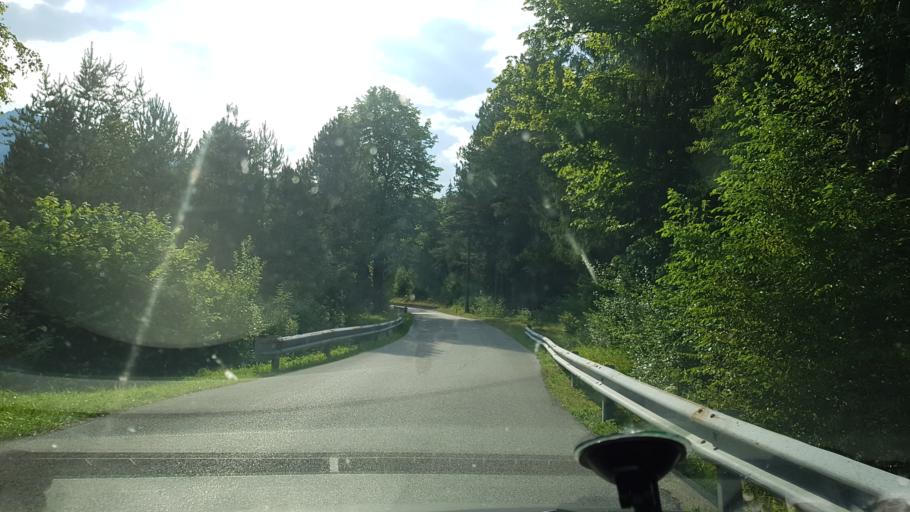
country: IT
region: Friuli Venezia Giulia
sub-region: Provincia di Udine
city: Prato
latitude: 46.3621
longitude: 13.3466
